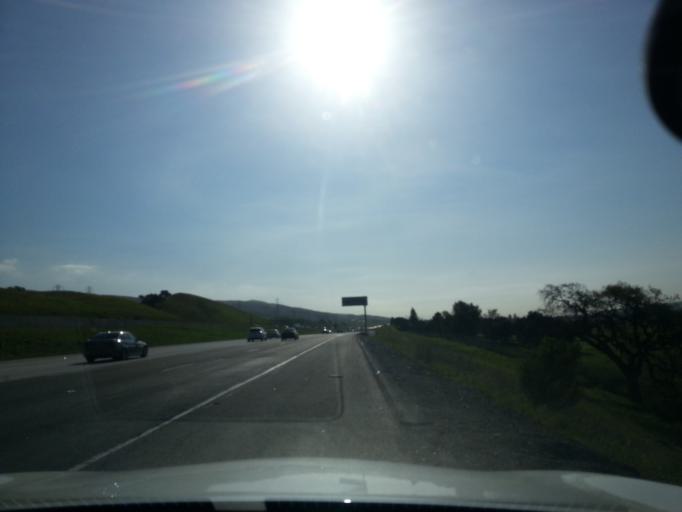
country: US
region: California
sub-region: Santa Clara County
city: Morgan Hill
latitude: 37.2006
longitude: -121.7084
